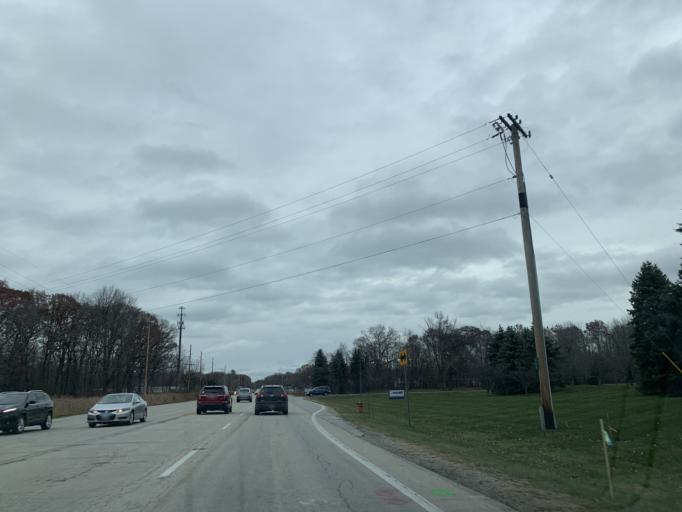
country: US
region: Indiana
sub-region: LaPorte County
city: Long Beach
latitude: 41.7325
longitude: -86.8261
